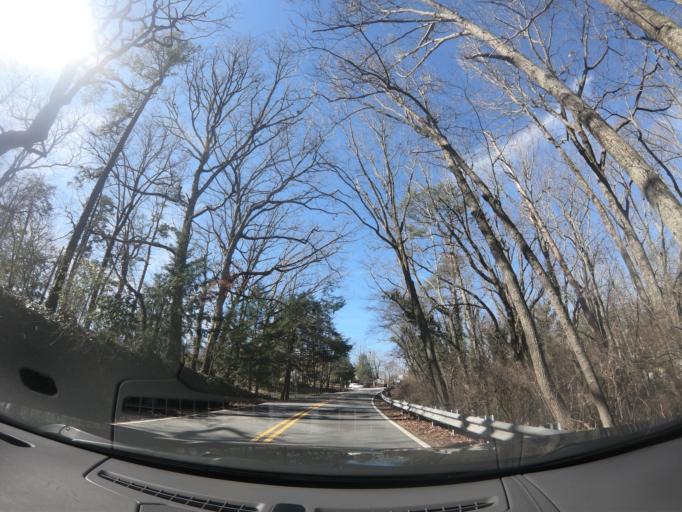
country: US
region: Georgia
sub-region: Walker County
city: Lookout Mountain
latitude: 34.9759
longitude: -85.3492
